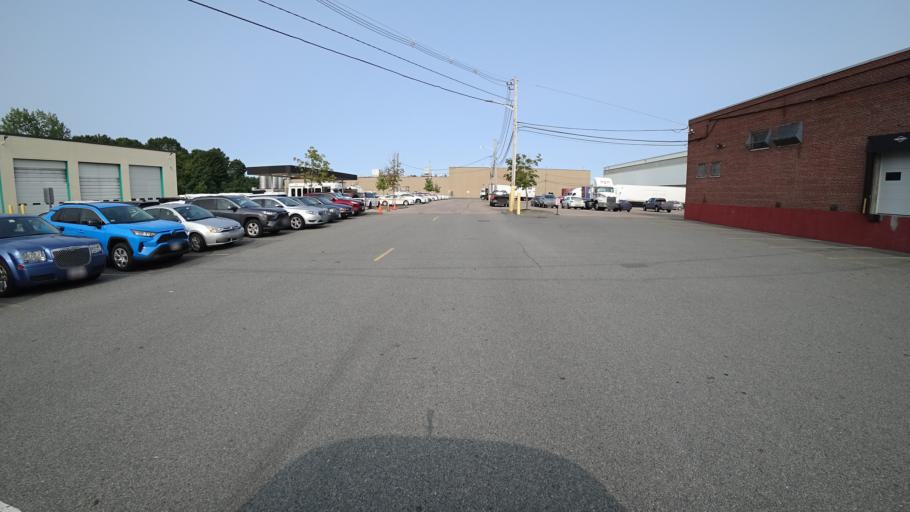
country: US
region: Massachusetts
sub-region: Norfolk County
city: Dedham
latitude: 42.2287
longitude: -71.1342
